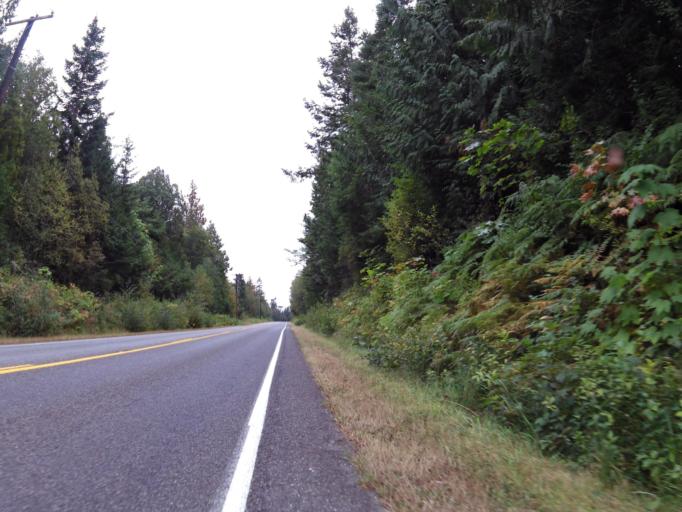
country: US
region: Washington
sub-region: Jefferson County
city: Port Ludlow
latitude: 47.9836
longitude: -122.7170
